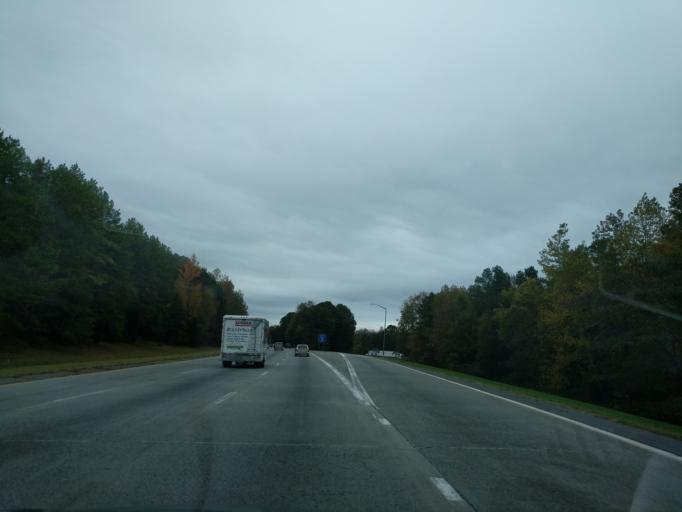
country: US
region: North Carolina
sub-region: Davidson County
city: Thomasville
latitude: 35.8390
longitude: -80.1379
